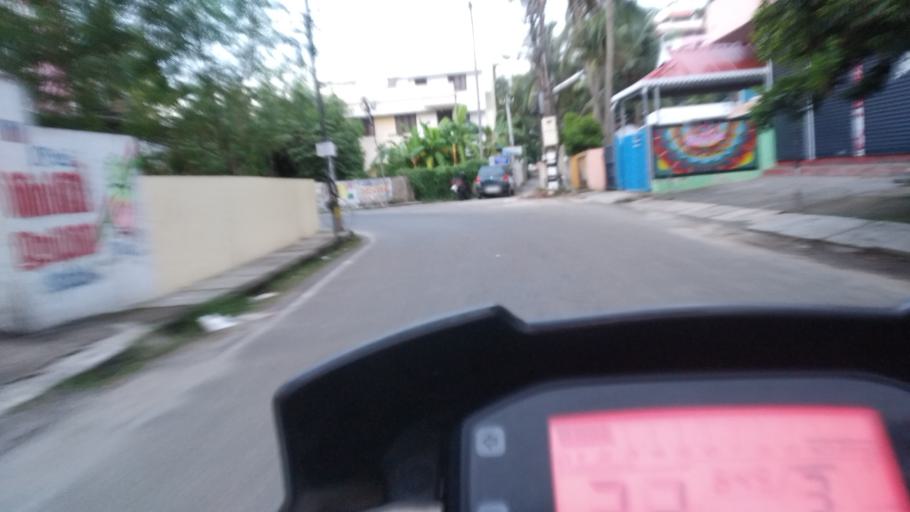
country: IN
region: Kerala
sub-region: Ernakulam
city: Elur
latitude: 10.0123
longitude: 76.2759
